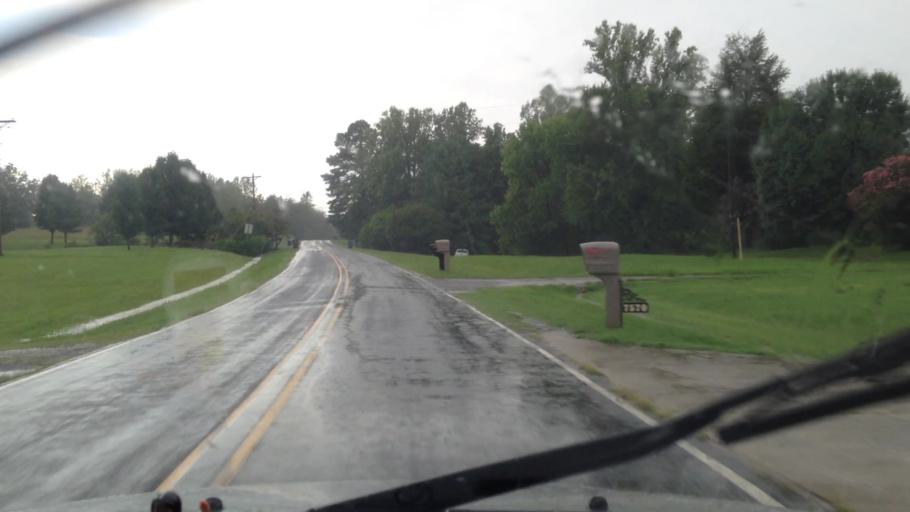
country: US
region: North Carolina
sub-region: Guilford County
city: Stokesdale
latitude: 36.2177
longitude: -80.0297
